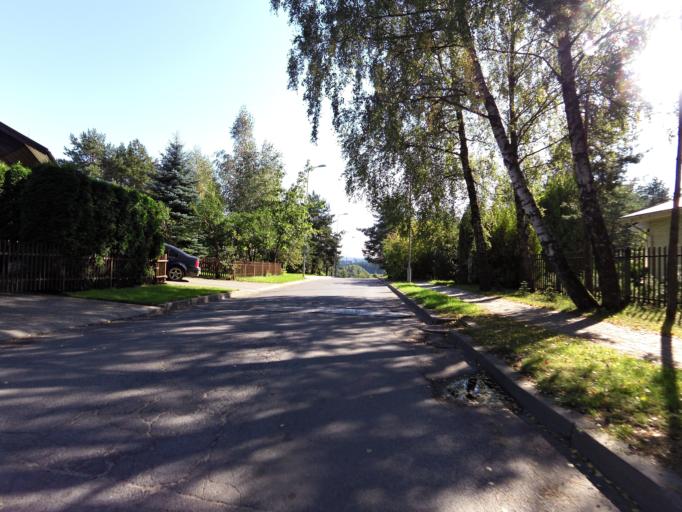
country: LT
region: Vilnius County
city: Lazdynai
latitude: 54.6749
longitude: 25.1944
